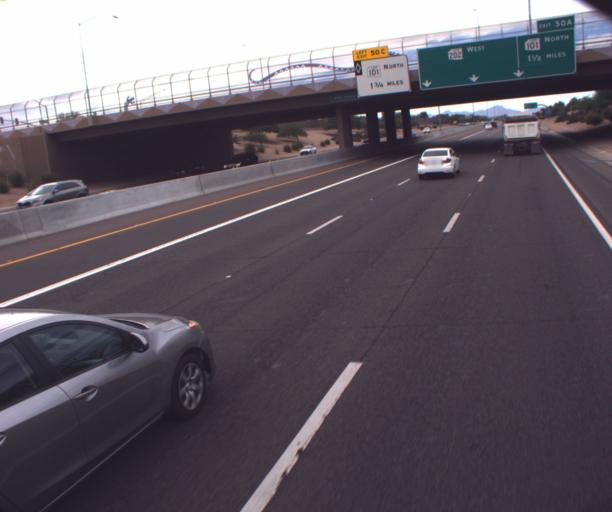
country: US
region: Arizona
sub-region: Maricopa County
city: Chandler
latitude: 33.2874
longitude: -111.8581
